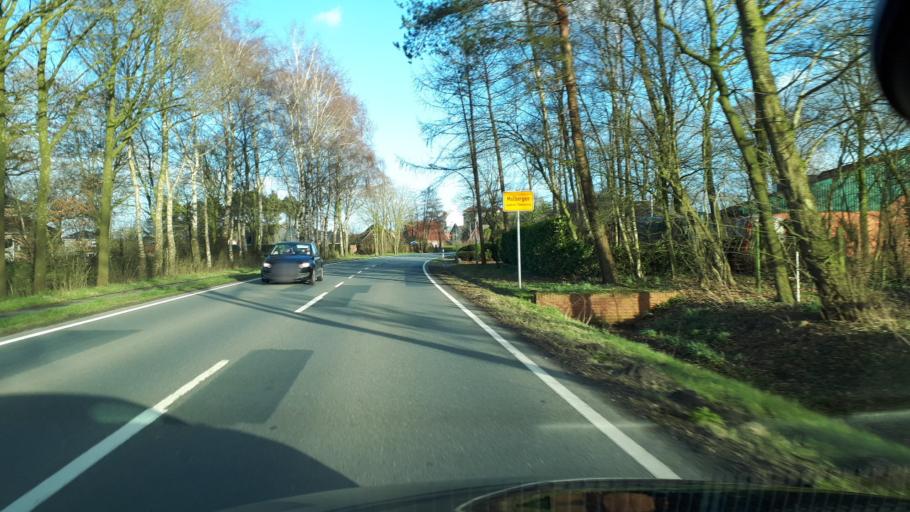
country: DE
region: Lower Saxony
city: Molbergen
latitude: 52.8657
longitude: 7.9085
